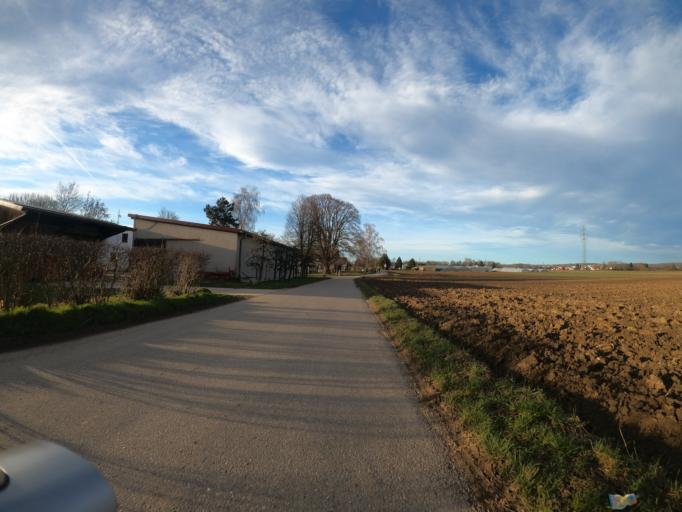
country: DE
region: Baden-Wuerttemberg
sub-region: Regierungsbezirk Stuttgart
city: Denkendorf
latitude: 48.7062
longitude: 9.3166
